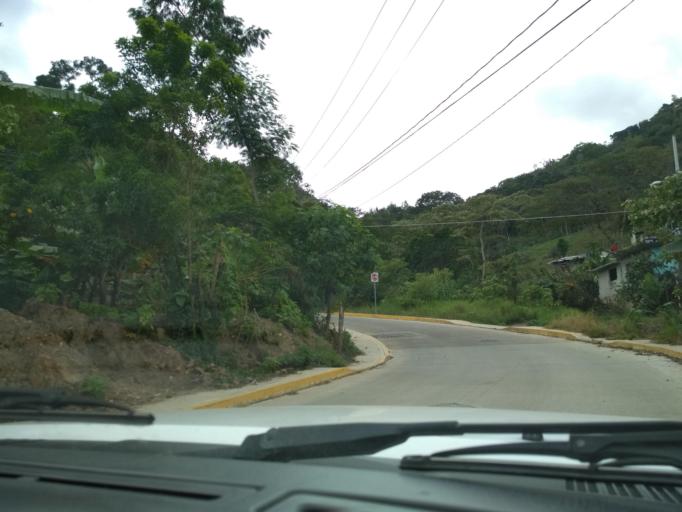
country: MX
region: Veracruz
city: El Castillo
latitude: 19.5805
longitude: -96.8670
